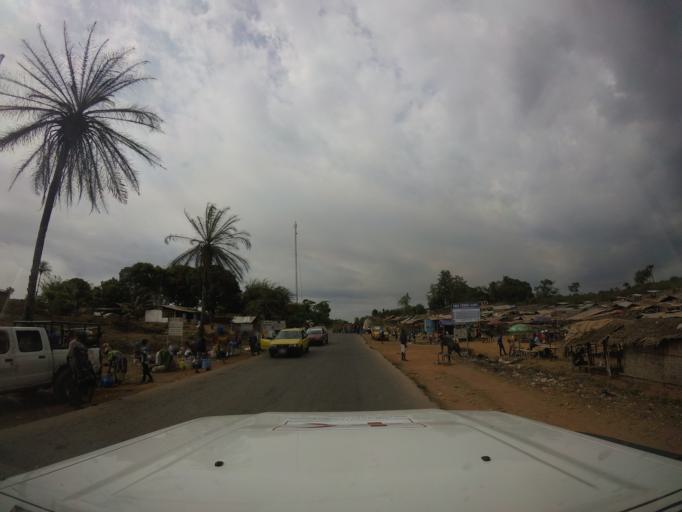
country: LR
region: Bomi
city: Tubmanburg
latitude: 6.5838
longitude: -10.8898
